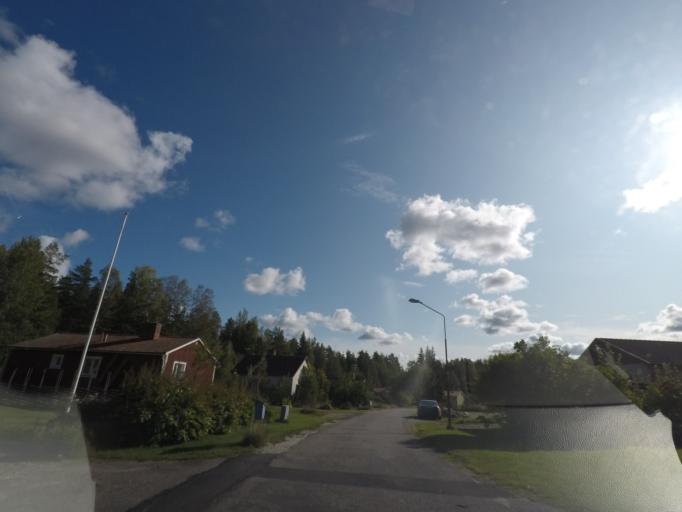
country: SE
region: Vaestmanland
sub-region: Skinnskattebergs Kommun
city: Skinnskatteberg
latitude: 59.8086
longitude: 15.5529
